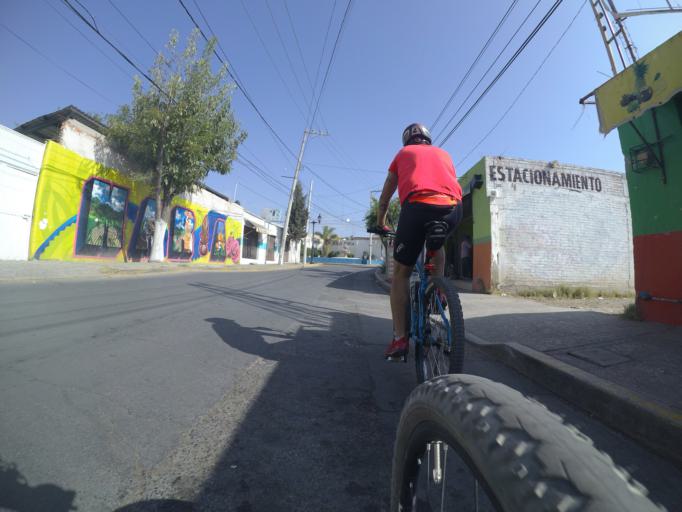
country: MX
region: Aguascalientes
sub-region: Jesus Maria
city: Jesus Maria
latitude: 21.9596
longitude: -102.3430
